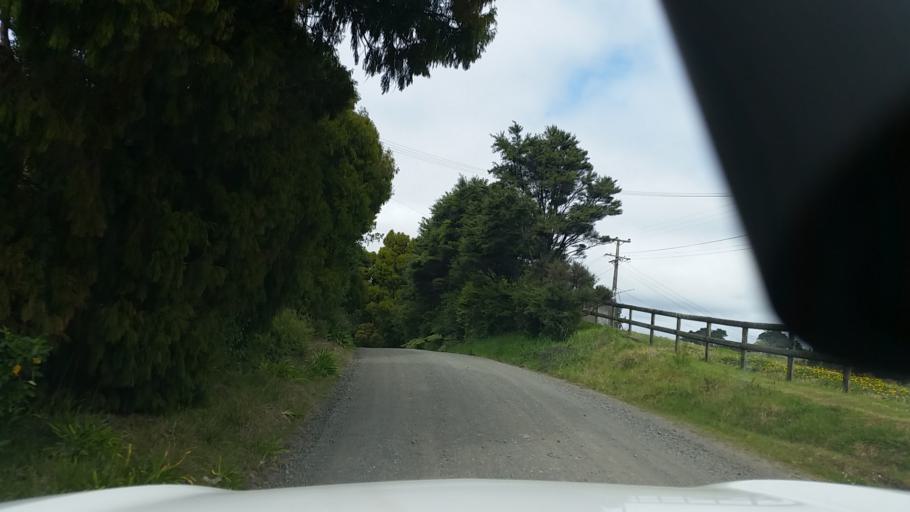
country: NZ
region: Auckland
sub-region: Auckland
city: Muriwai Beach
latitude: -36.8449
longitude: 174.5108
